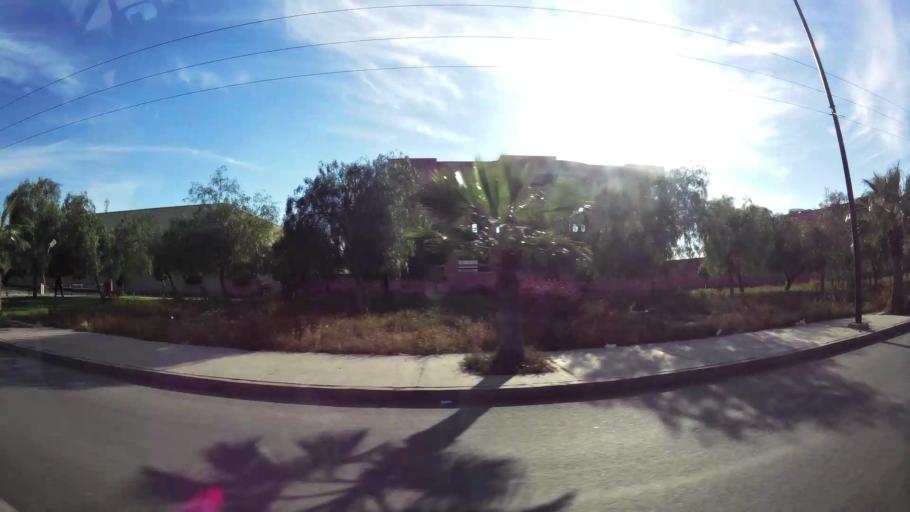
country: MA
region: Marrakech-Tensift-Al Haouz
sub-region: Marrakech
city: Marrakesh
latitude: 31.6836
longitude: -8.0509
